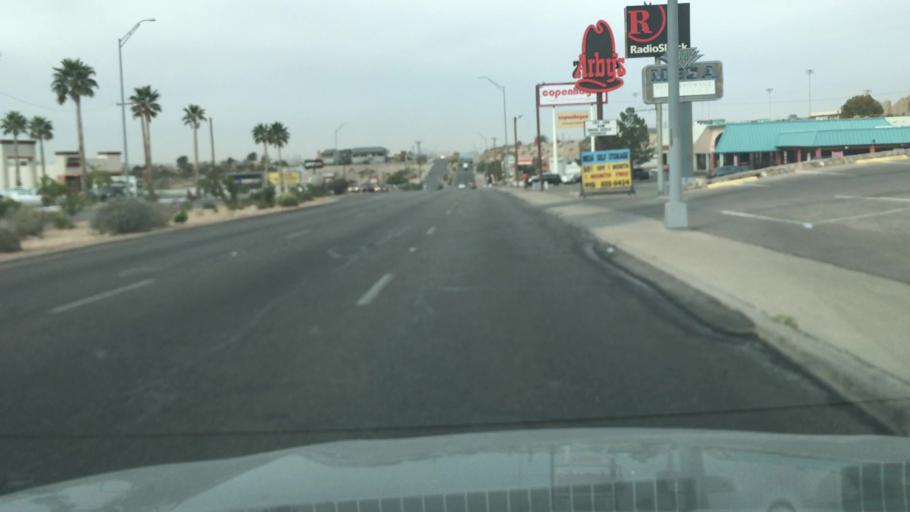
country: US
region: New Mexico
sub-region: Dona Ana County
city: Sunland Park
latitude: 31.8334
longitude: -106.5382
